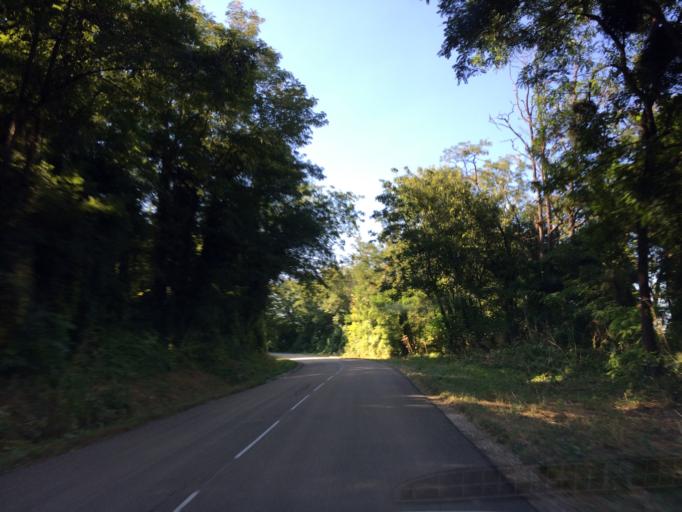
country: FR
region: Bourgogne
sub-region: Departement de l'Yonne
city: Cheny
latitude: 47.9286
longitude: 3.5089
